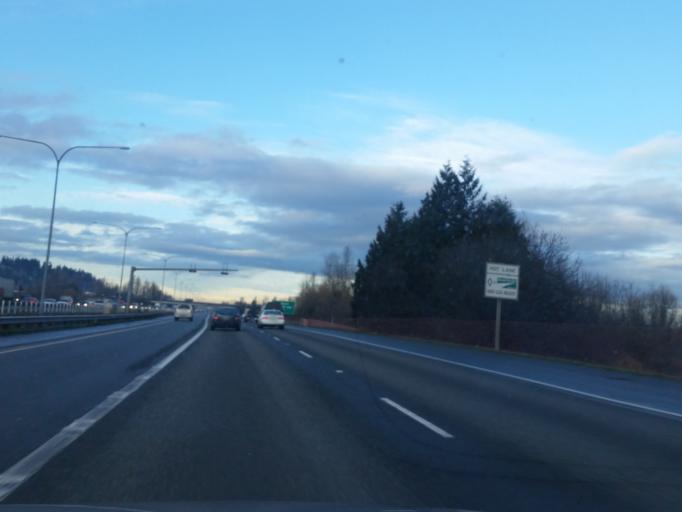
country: US
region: Washington
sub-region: King County
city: Auburn
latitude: 47.3167
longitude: -122.2448
